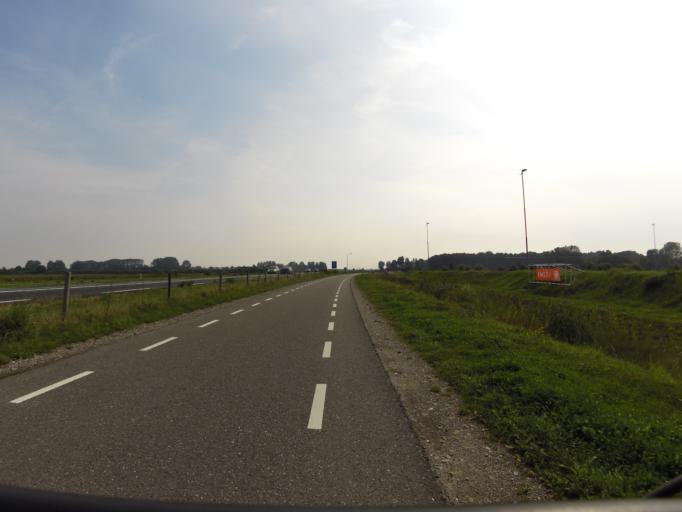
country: NL
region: Zeeland
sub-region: Gemeente Middelburg
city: Middelburg
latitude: 51.5499
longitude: 3.6029
